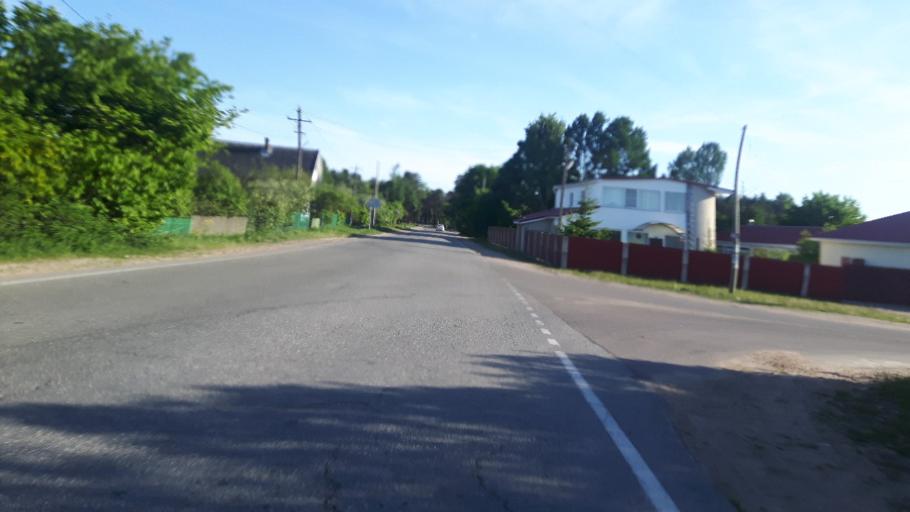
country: RU
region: Leningrad
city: Vistino
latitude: 59.7751
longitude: 28.4770
